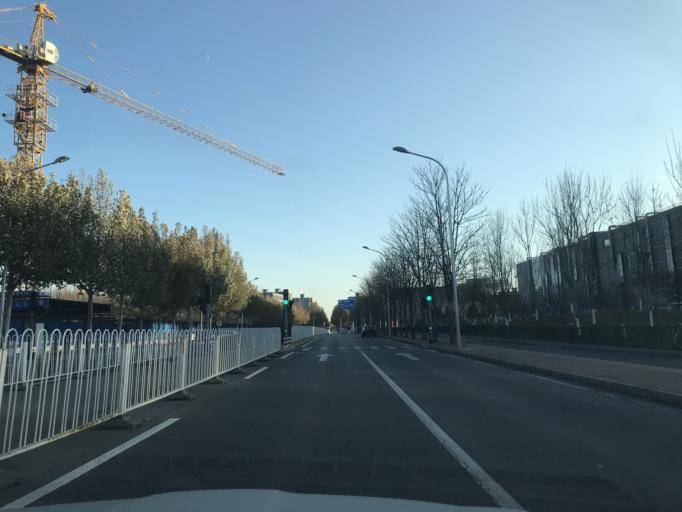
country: CN
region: Beijing
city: Xibeiwang
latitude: 40.0702
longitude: 116.2464
